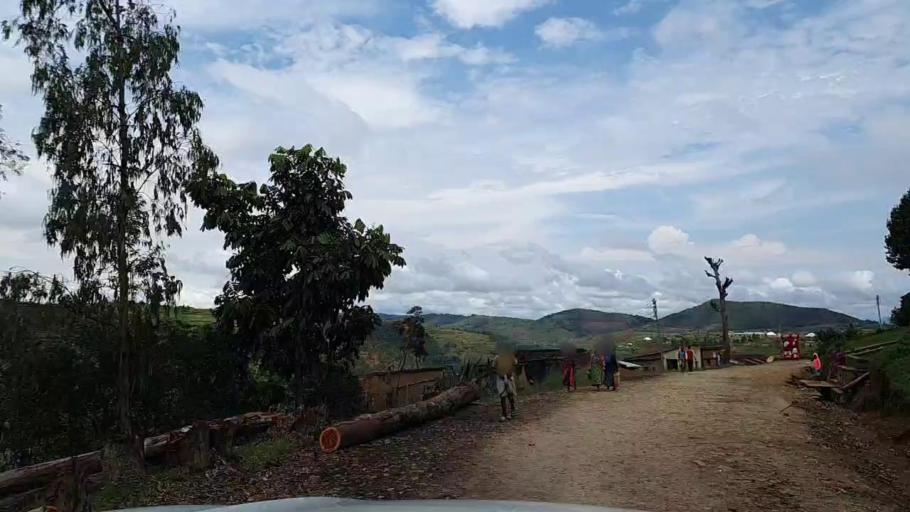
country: RW
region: Southern Province
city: Gikongoro
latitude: -2.3330
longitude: 29.5238
